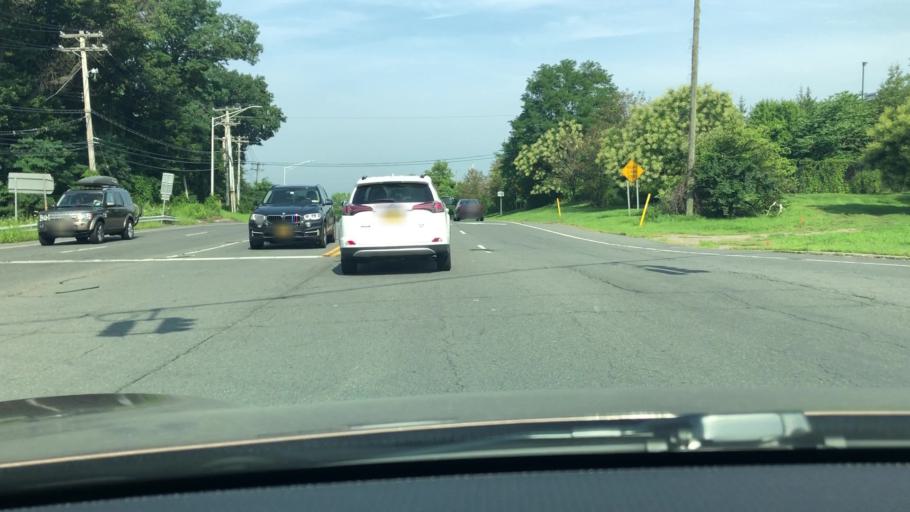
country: US
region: New York
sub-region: Westchester County
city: Elmsford
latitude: 41.0752
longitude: -73.8047
